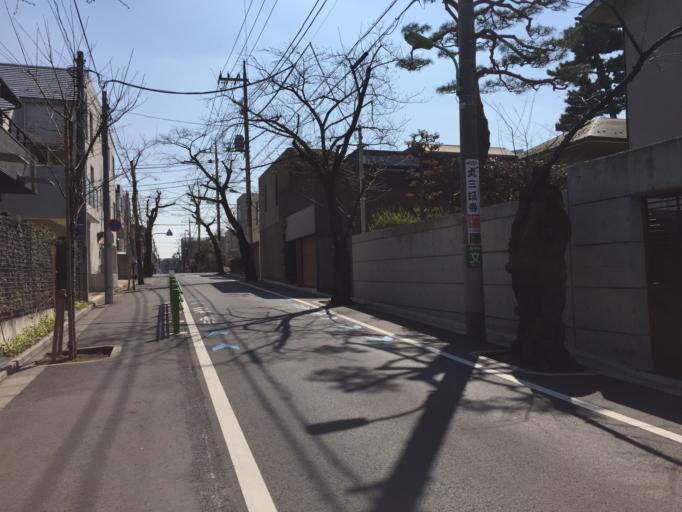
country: JP
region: Tokyo
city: Tokyo
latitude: 35.6242
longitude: 139.6470
